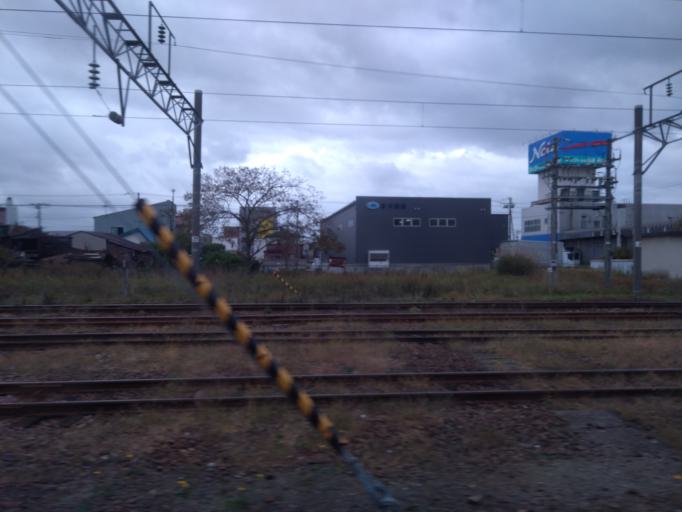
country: JP
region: Hokkaido
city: Hakodate
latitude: 41.7792
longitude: 140.7289
